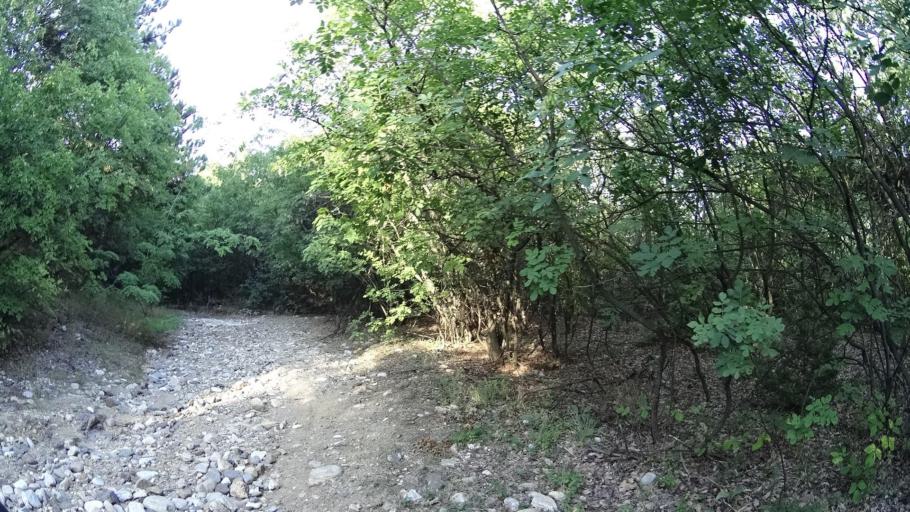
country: BG
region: Plovdiv
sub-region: Obshtina Plovdiv
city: Plovdiv
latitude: 42.0551
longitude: 24.6946
